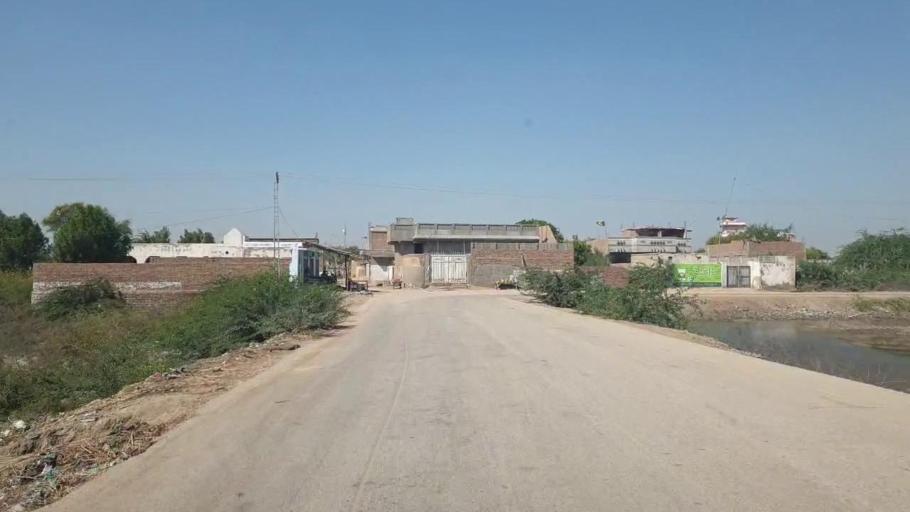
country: PK
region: Sindh
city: Talhar
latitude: 24.8788
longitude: 68.8177
